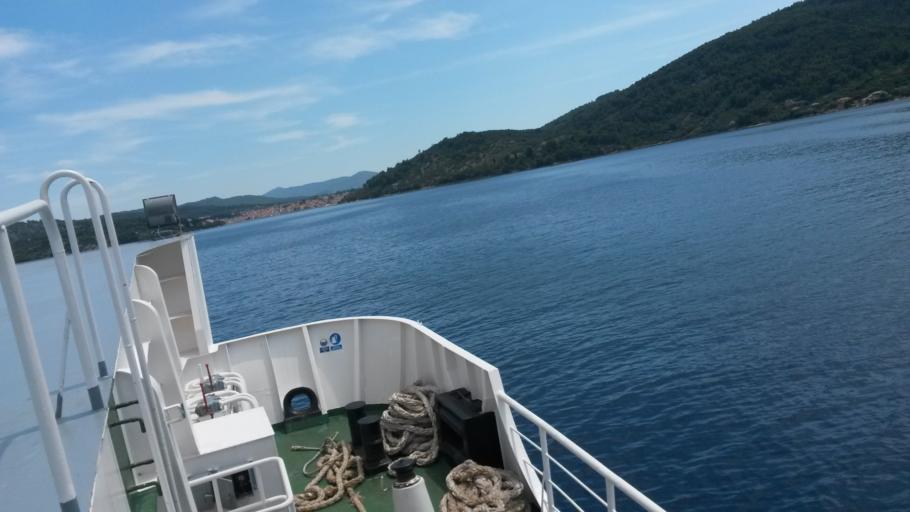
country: HR
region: Dubrovacko-Neretvanska
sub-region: Grad Dubrovnik
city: Vela Luka
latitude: 42.9640
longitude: 16.6838
